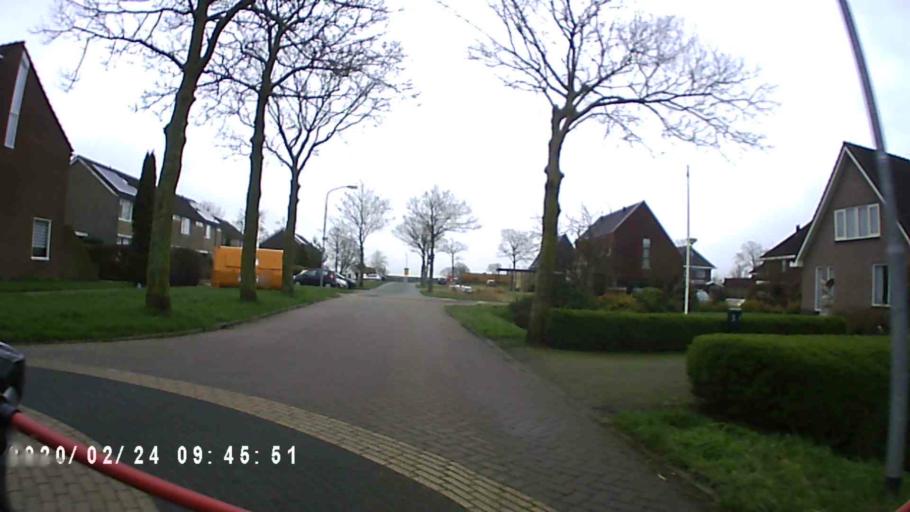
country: NL
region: Groningen
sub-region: Gemeente Winsum
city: Winsum
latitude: 53.2926
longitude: 6.5384
